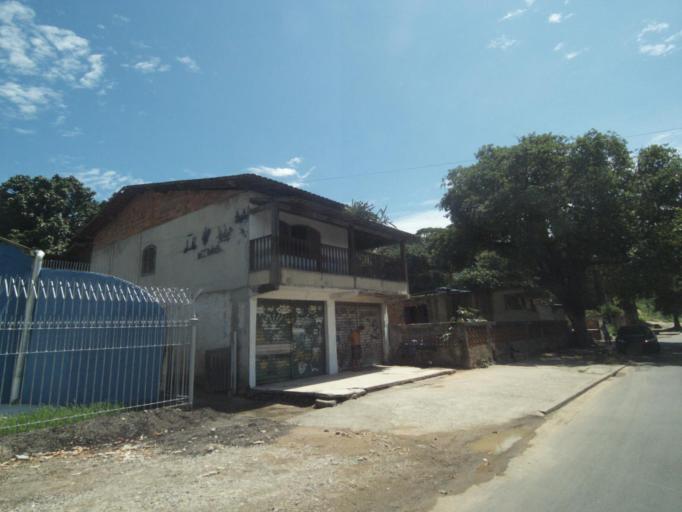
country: BR
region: Rio de Janeiro
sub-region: Sao Goncalo
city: Sao Goncalo
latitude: -22.9022
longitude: -42.9856
